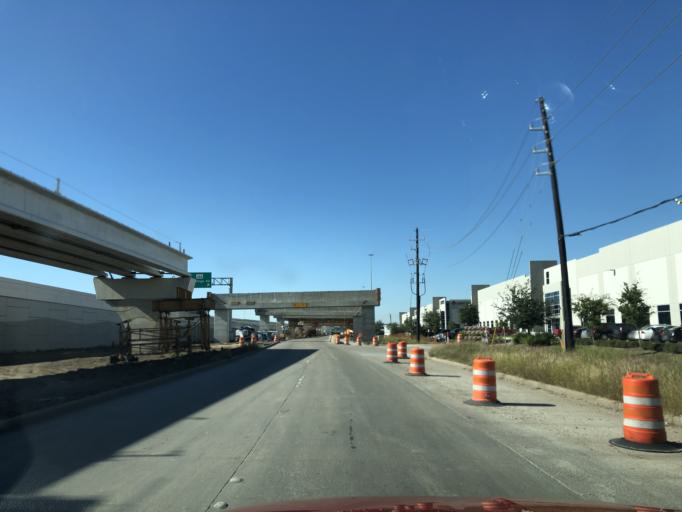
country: US
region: Texas
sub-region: Brazoria County
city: Brookside Village
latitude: 29.5985
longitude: -95.3690
